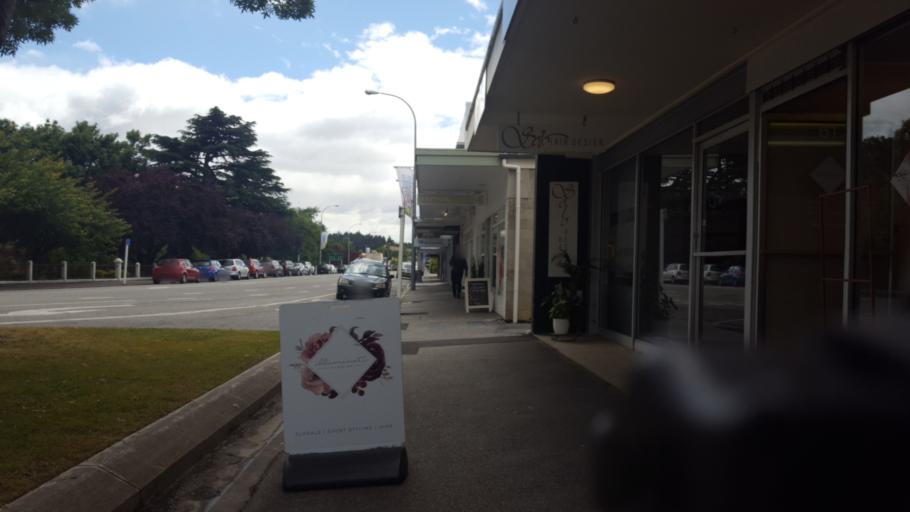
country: NZ
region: Otago
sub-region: Queenstown-Lakes District
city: Wanaka
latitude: -45.2554
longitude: 169.3932
